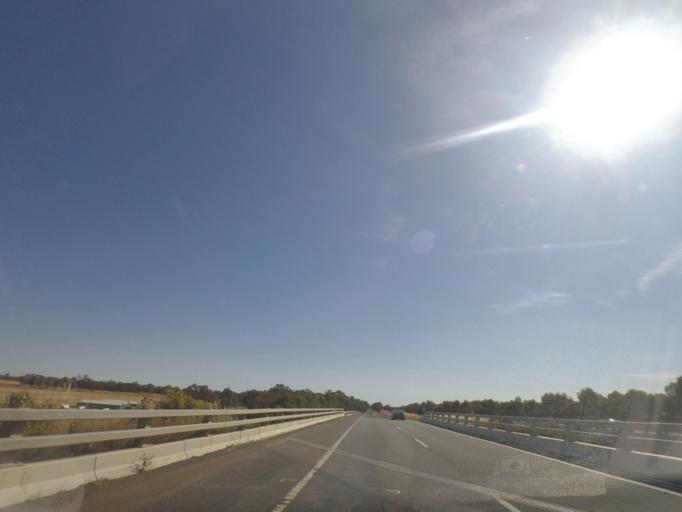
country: AU
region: Victoria
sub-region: Greater Shepparton
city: Shepparton
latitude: -36.6796
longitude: 145.2400
